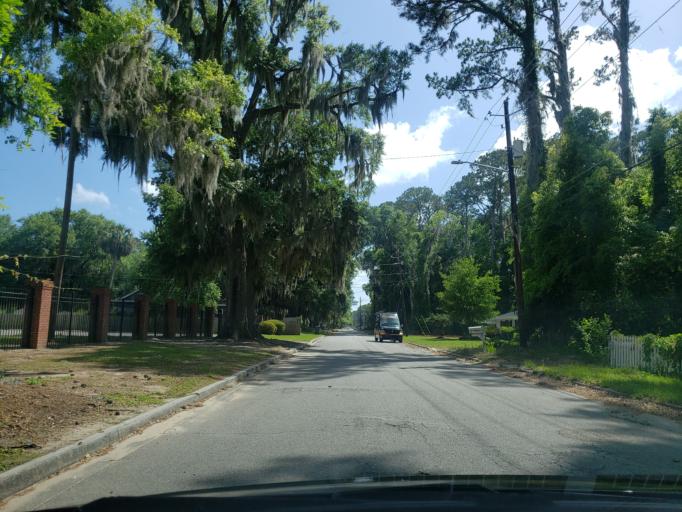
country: US
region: Georgia
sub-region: Chatham County
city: Thunderbolt
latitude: 32.0199
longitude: -81.0626
